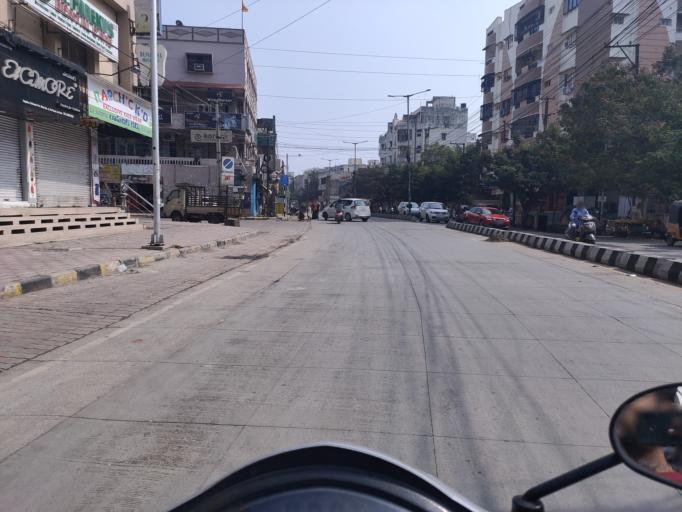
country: IN
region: Telangana
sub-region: Hyderabad
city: Malkajgiri
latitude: 17.4401
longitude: 78.4832
